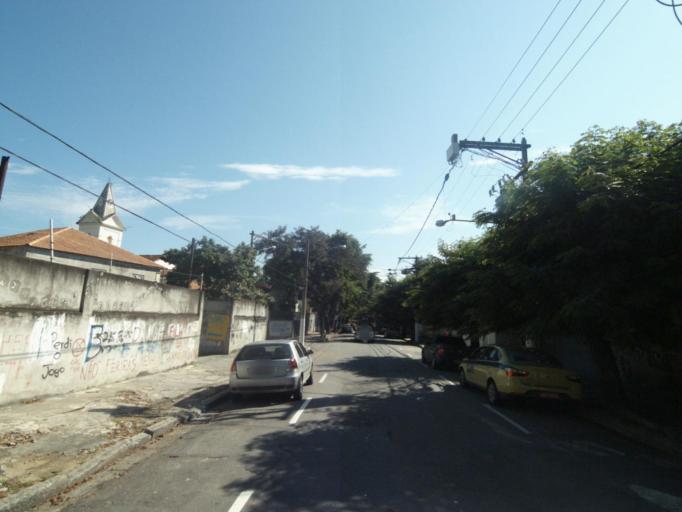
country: BR
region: Rio de Janeiro
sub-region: Niteroi
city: Niteroi
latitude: -22.9008
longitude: -43.1308
